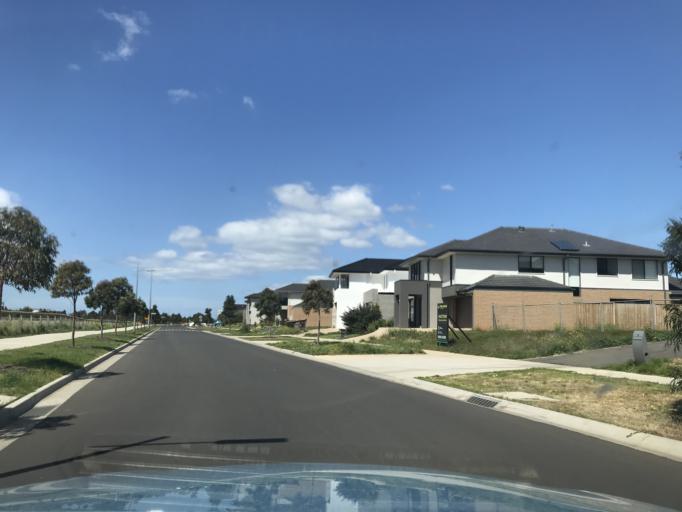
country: AU
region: Victoria
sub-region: Wyndham
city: Williams Landing
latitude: -37.8622
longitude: 144.7371
